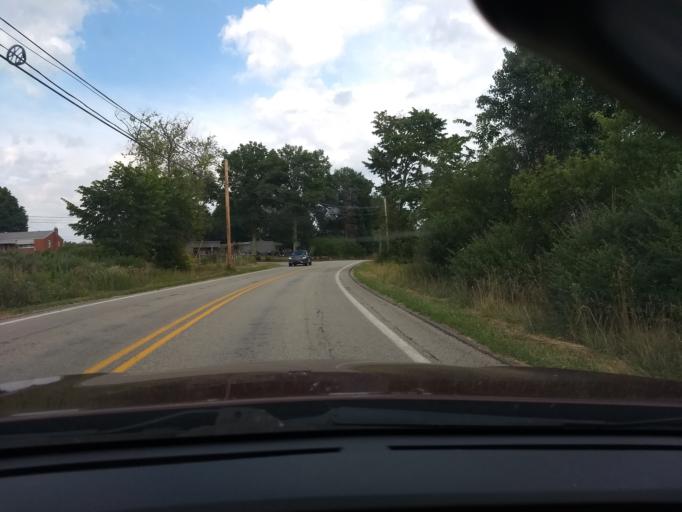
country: US
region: Pennsylvania
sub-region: Allegheny County
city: Curtisville
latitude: 40.6610
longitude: -79.8546
